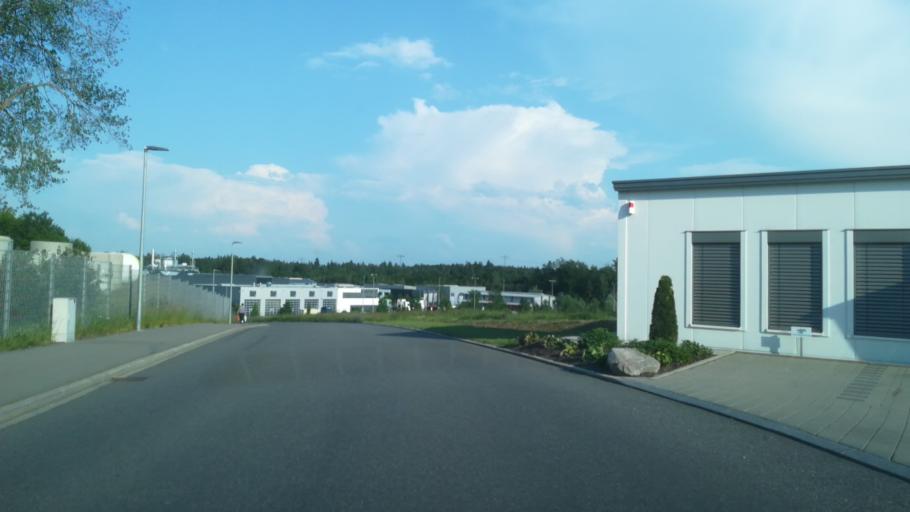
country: DE
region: Baden-Wuerttemberg
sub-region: Freiburg Region
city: Steisslingen
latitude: 47.7772
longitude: 8.9095
